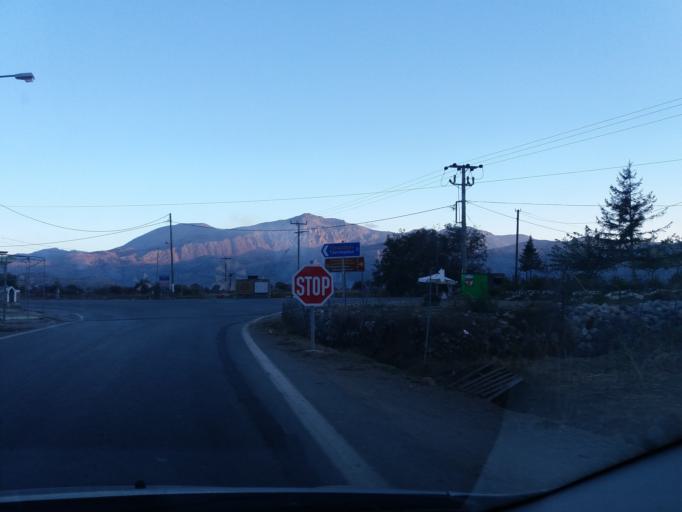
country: GR
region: Crete
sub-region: Nomos Irakleiou
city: Mokhos
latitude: 35.1973
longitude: 25.4624
